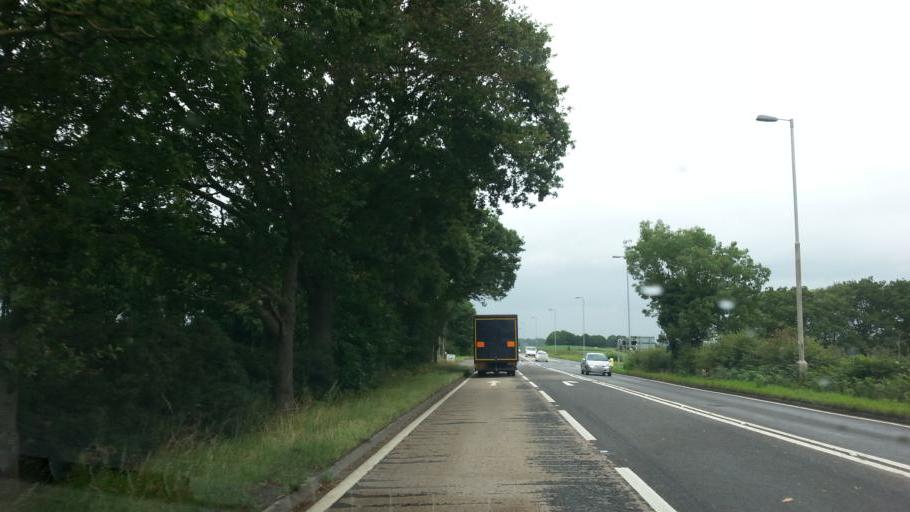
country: GB
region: England
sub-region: Nottinghamshire
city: Bilsthorpe
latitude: 53.1503
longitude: -1.0474
